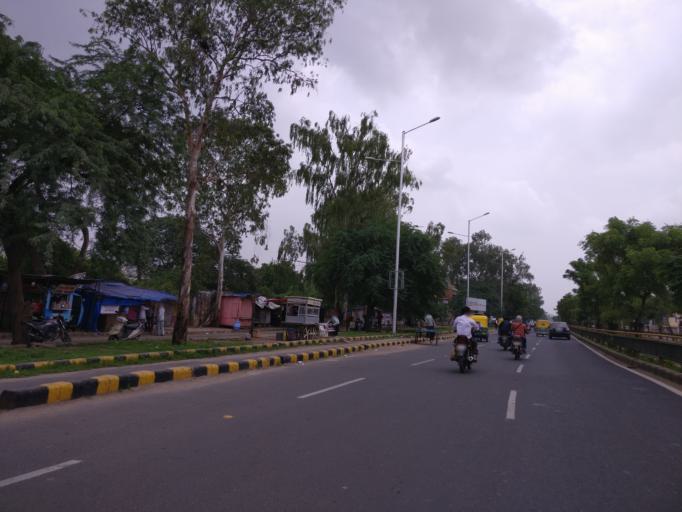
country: IN
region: Gujarat
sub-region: Gandhinagar
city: Adalaj
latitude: 23.1077
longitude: 72.5854
